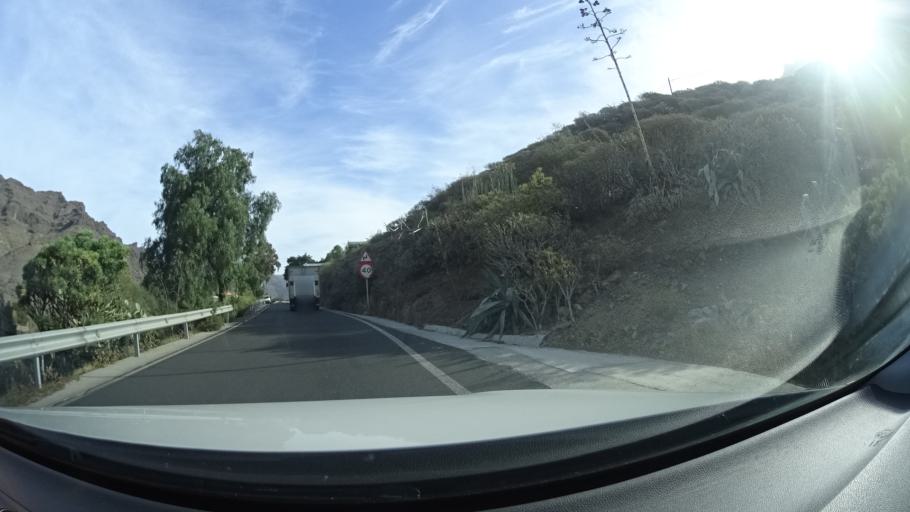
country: ES
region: Canary Islands
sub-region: Provincia de Las Palmas
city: Mogan
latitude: 27.8702
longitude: -15.7332
